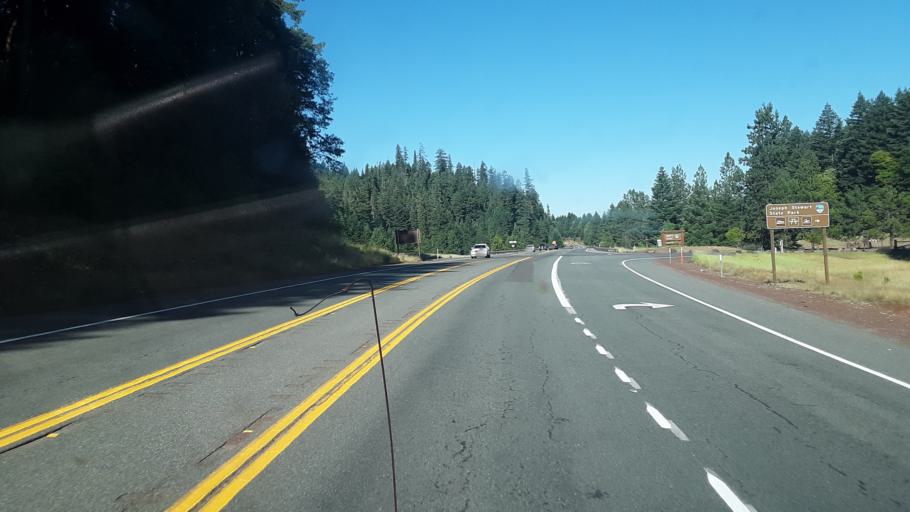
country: US
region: Oregon
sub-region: Jackson County
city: Shady Cove
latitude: 42.6745
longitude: -122.6245
